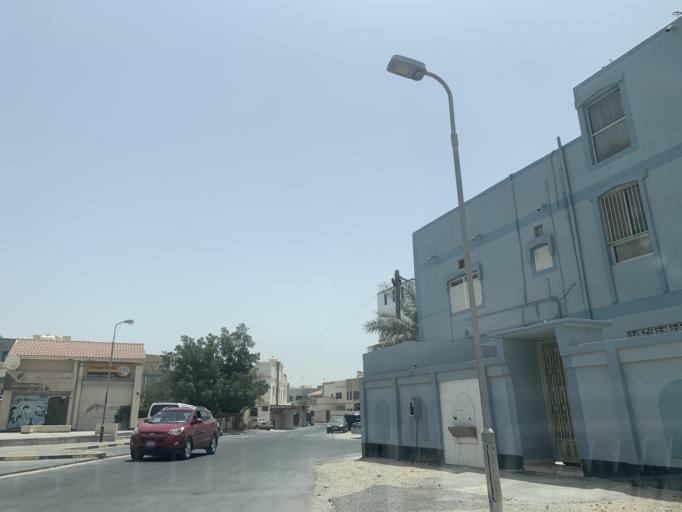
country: BH
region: Northern
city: Madinat `Isa
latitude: 26.1548
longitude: 50.5236
